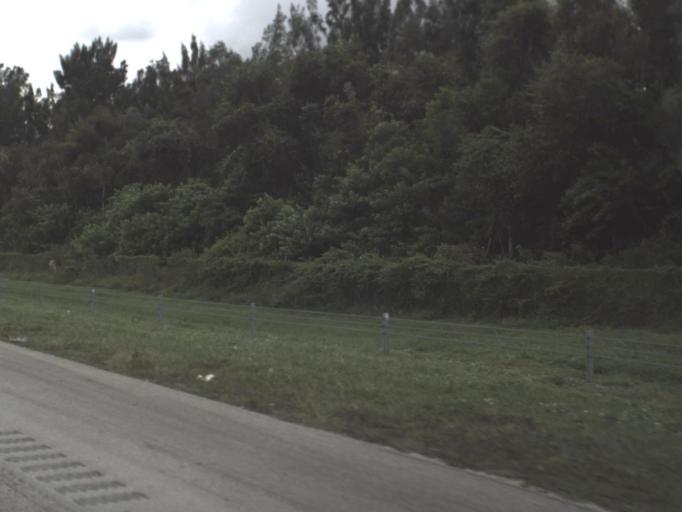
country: US
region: Florida
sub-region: Palm Beach County
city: Plantation Mobile Home Park
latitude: 26.7252
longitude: -80.1356
